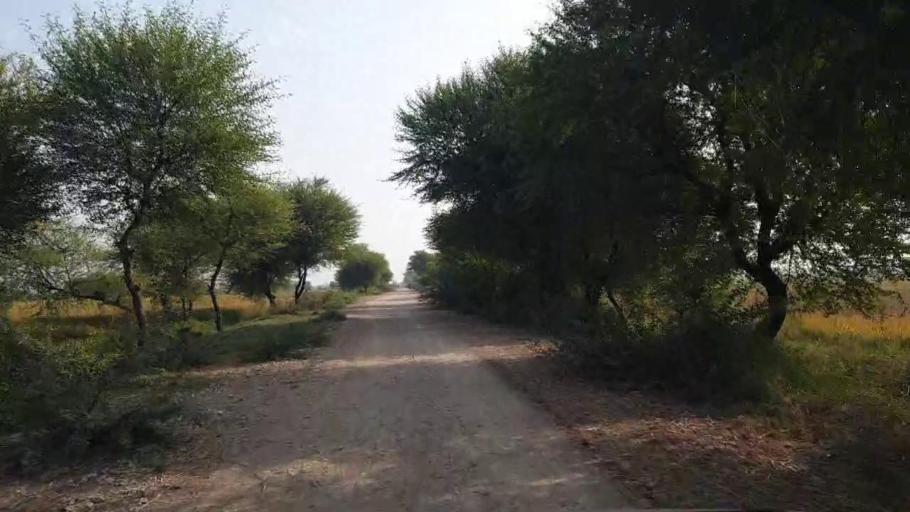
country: PK
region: Sindh
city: Talhar
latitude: 24.8939
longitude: 68.8727
